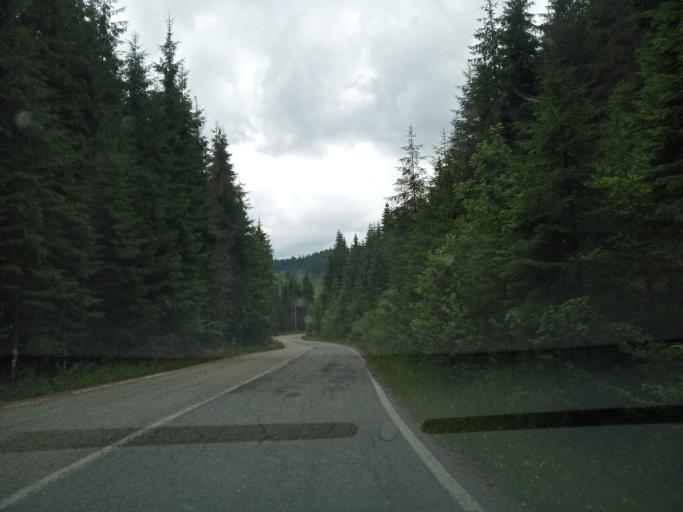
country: RO
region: Valcea
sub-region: Comuna Voineasa
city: Voineasa
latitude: 45.4265
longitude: 23.7388
